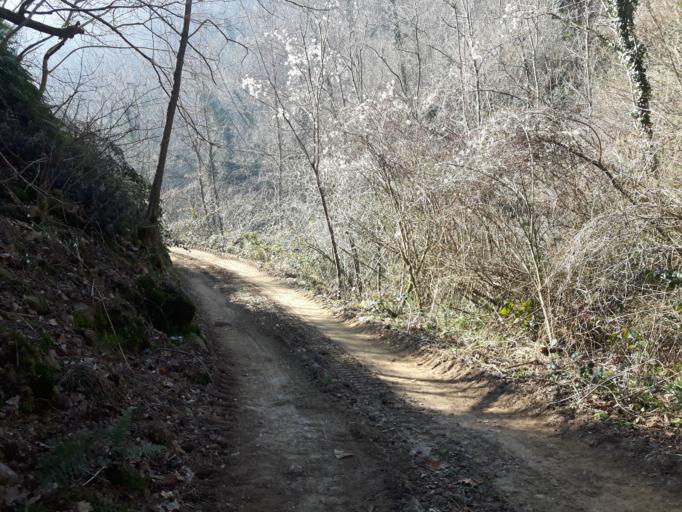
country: IT
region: Veneto
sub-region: Provincia di Padova
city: Vo
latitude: 45.3527
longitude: 11.6628
